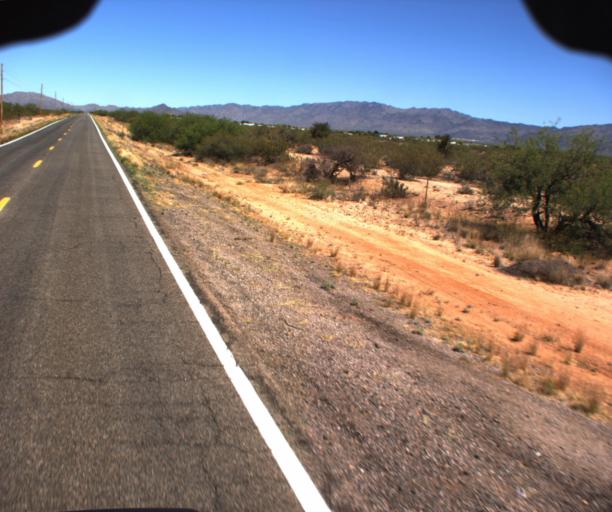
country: US
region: Arizona
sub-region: Yavapai County
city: Congress
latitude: 34.0934
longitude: -112.8281
